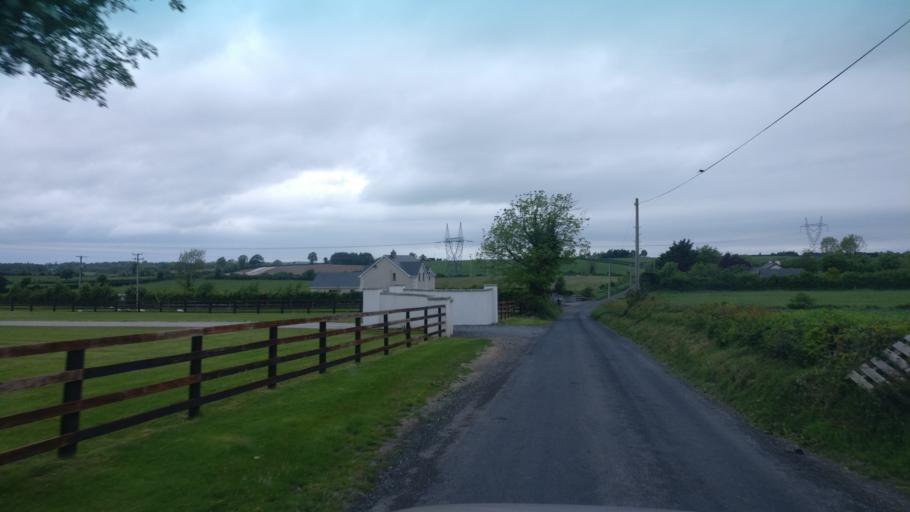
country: IE
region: Connaught
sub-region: County Galway
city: Portumna
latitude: 53.1242
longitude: -8.2908
